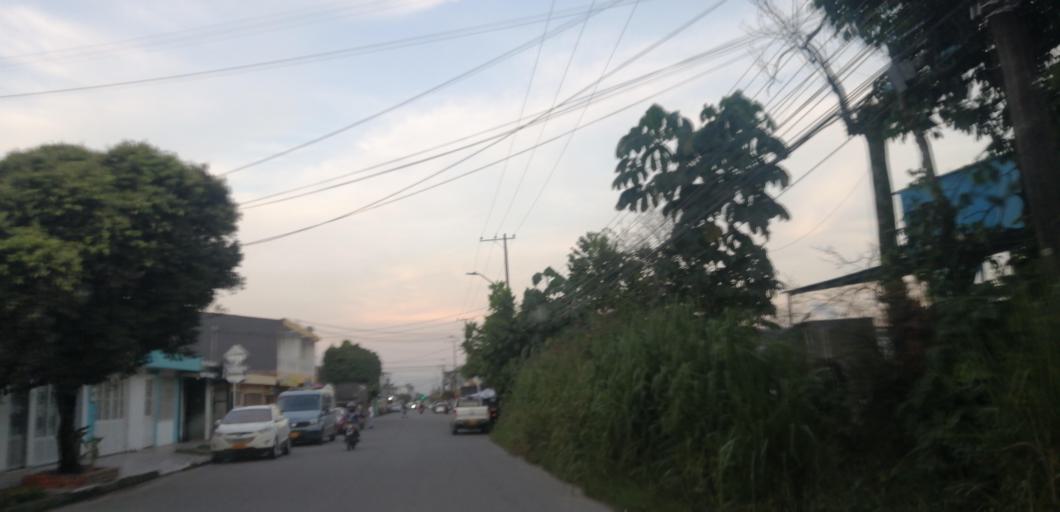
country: CO
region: Meta
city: Acacias
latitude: 3.9921
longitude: -73.7635
